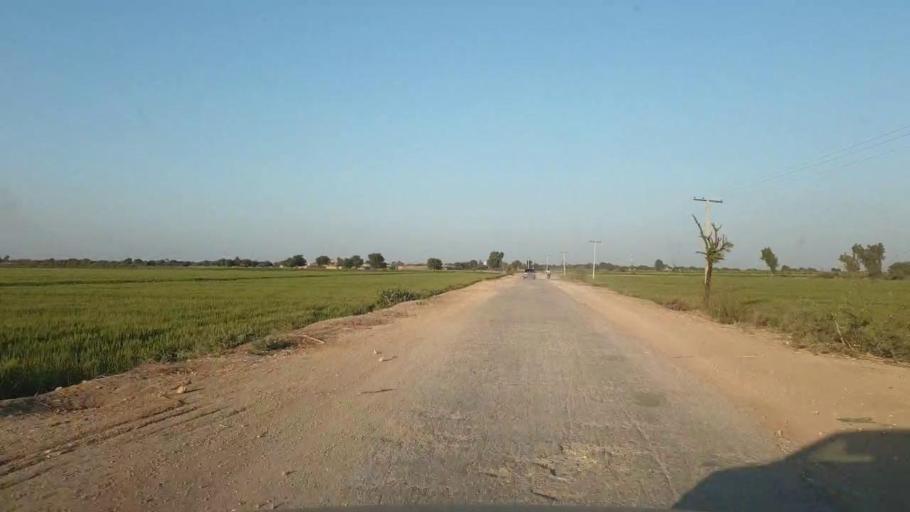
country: PK
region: Sindh
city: Tando Allahyar
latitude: 25.3828
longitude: 68.7529
